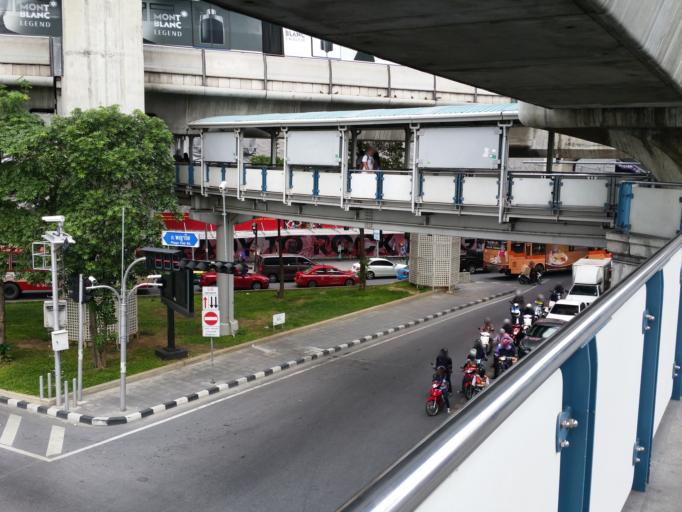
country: TH
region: Bangkok
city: Pathum Wan
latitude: 13.7457
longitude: 100.5313
